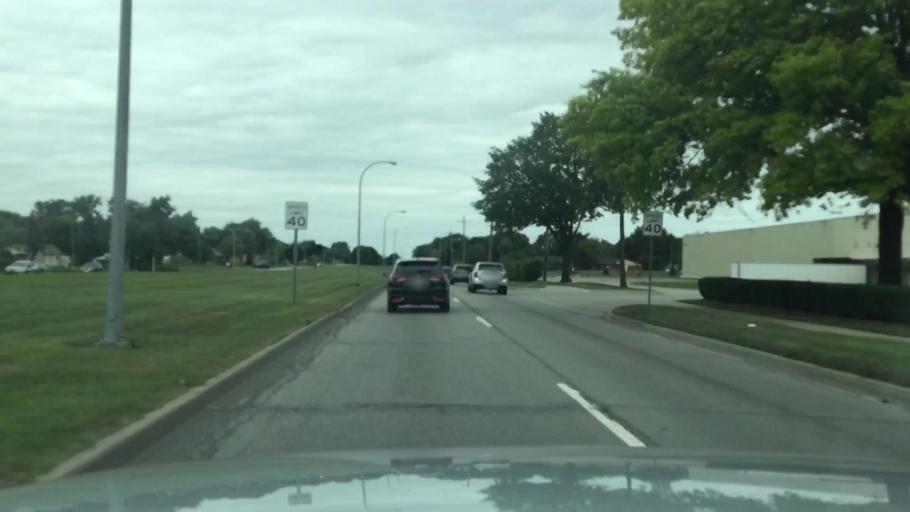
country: US
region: Michigan
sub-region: Macomb County
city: Center Line
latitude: 42.4915
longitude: -83.0478
